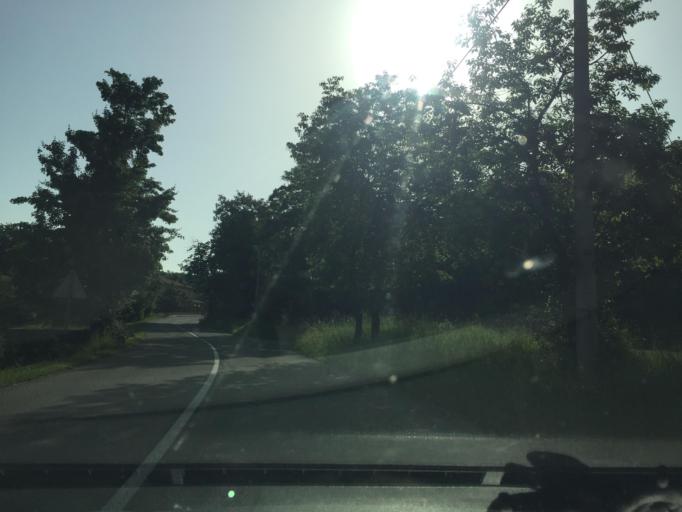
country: HR
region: Primorsko-Goranska
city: Matulji
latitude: 45.4167
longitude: 14.3083
